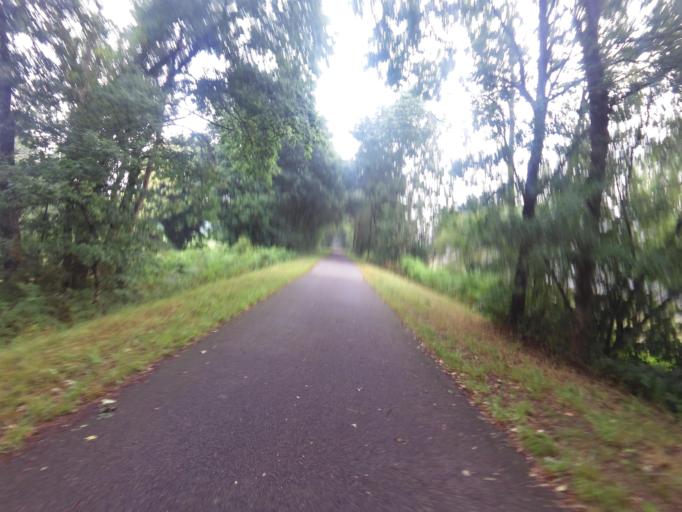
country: FR
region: Brittany
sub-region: Departement du Morbihan
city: Guillac
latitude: 47.8899
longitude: -2.4360
